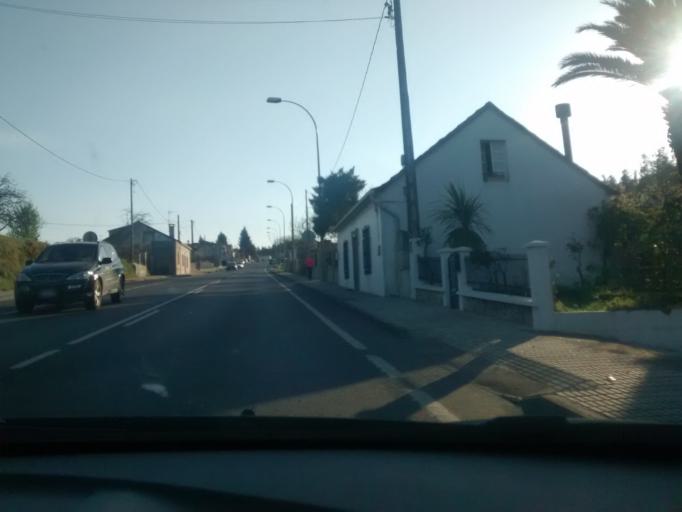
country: ES
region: Galicia
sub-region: Provincia de Pontevedra
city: A Estrada
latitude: 42.6933
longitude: -8.4676
